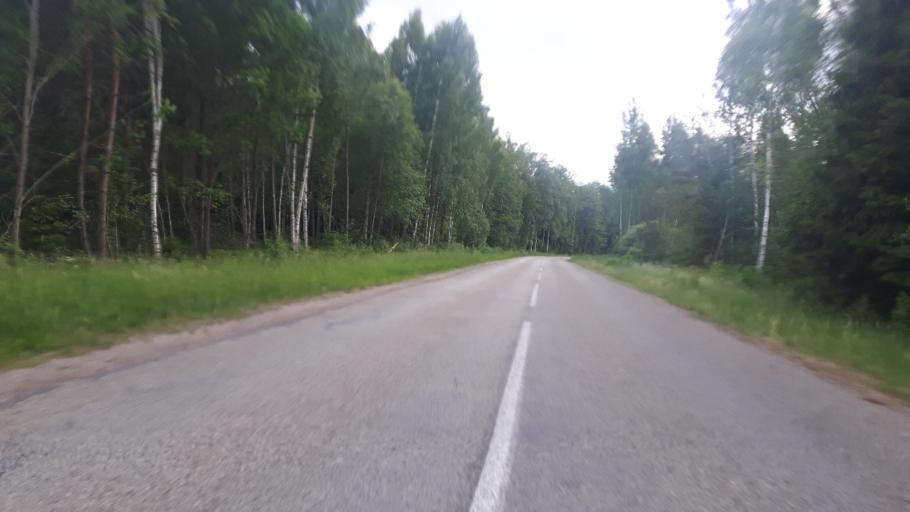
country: LV
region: Engure
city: Smarde
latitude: 57.0279
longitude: 23.3584
